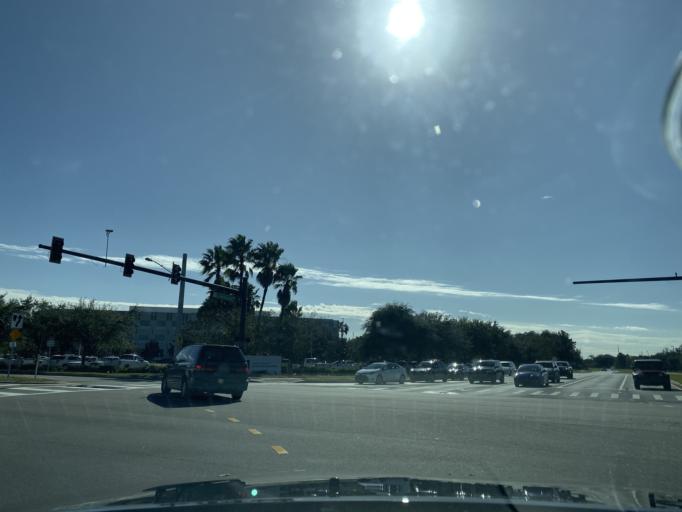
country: US
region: Florida
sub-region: Orange County
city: Azalea Park
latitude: 28.5102
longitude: -81.2566
